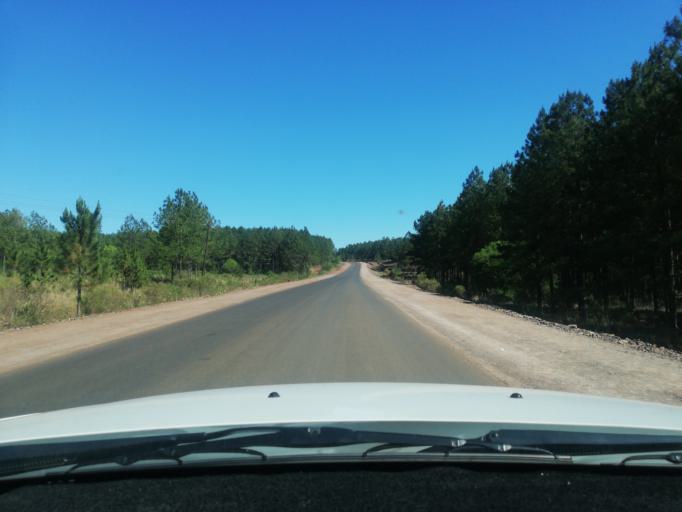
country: AR
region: Misiones
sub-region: Departamento de Candelaria
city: Candelaria
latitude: -27.5255
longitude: -55.7229
